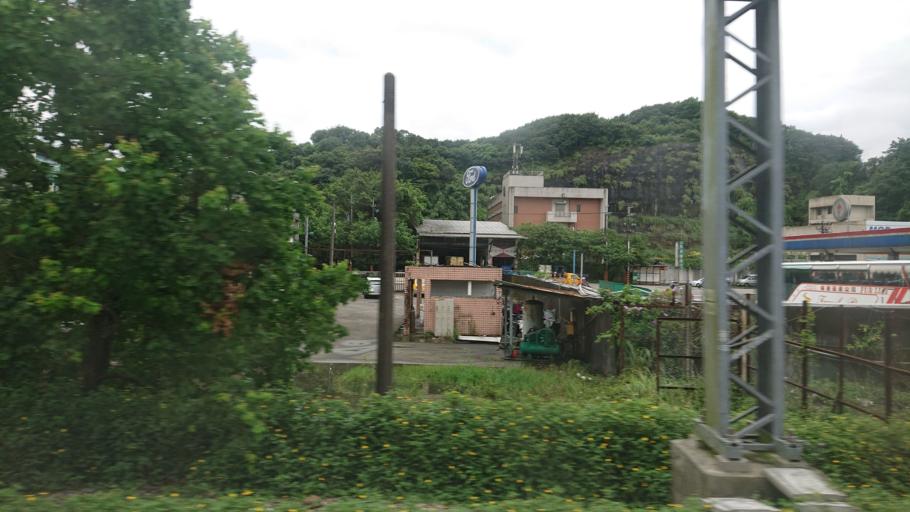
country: TW
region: Taiwan
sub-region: Keelung
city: Keelung
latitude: 25.1042
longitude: 121.7256
